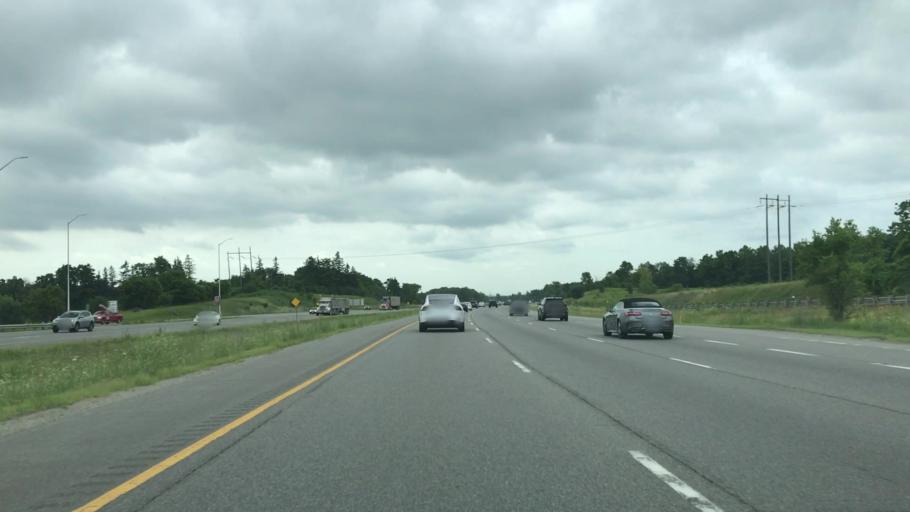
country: CA
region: Ontario
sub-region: York
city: Richmond Hill
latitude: 43.9379
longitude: -79.3896
